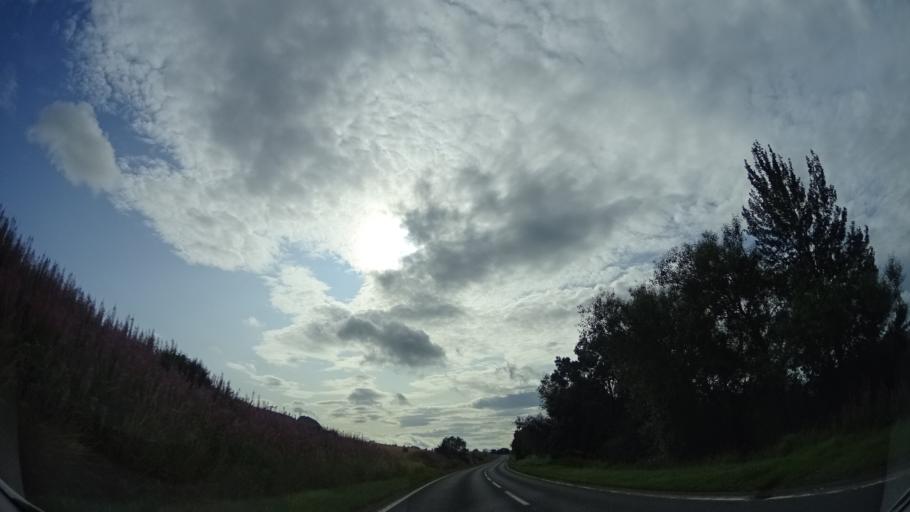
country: GB
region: Scotland
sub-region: Highland
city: Muir of Ord
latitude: 57.5608
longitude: -4.5542
